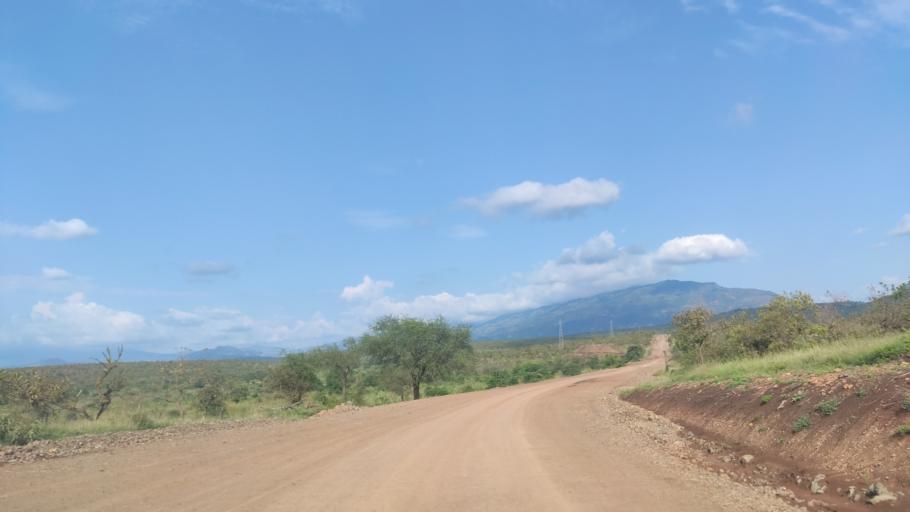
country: ET
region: Southern Nations, Nationalities, and People's Region
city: Felege Neway
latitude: 6.4339
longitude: 37.2662
